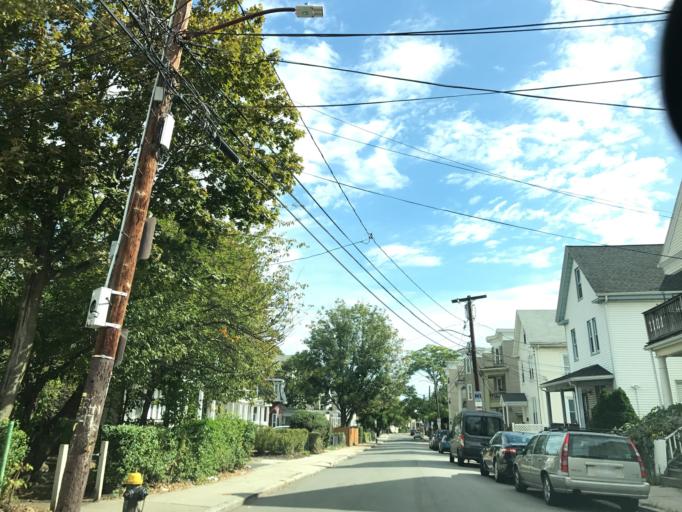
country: US
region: Massachusetts
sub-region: Norfolk County
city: Brookline
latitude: 42.3543
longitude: -71.1293
